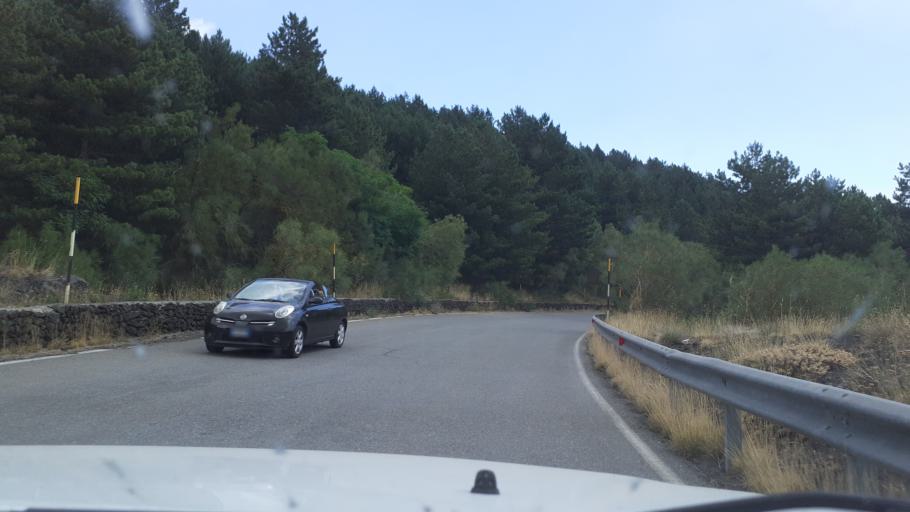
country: IT
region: Sicily
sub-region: Catania
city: Nicolosi
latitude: 37.6984
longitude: 15.0155
